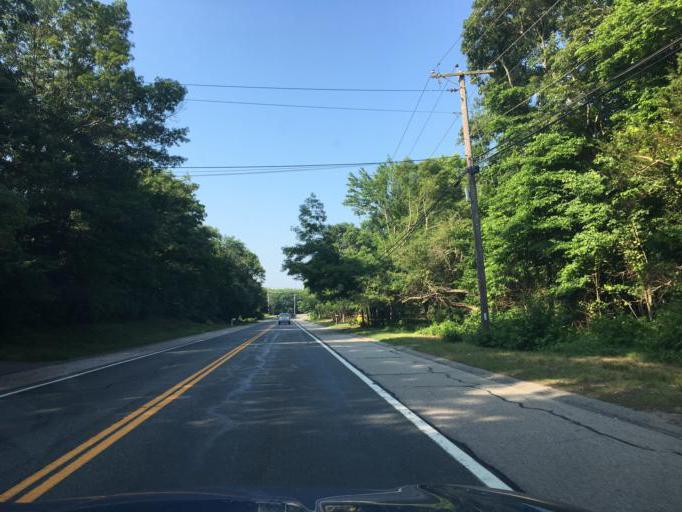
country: US
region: Rhode Island
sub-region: Washington County
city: Kingston
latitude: 41.5017
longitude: -71.5623
